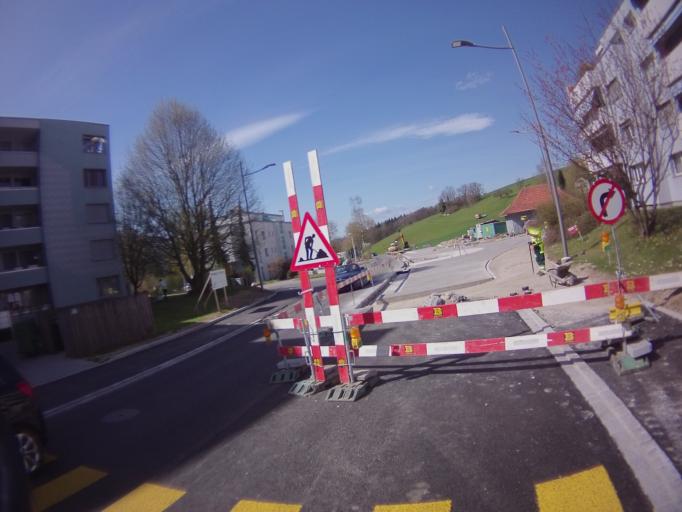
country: CH
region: Aargau
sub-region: Bezirk Baden
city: Niederrohrdorf
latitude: 47.4246
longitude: 8.3112
